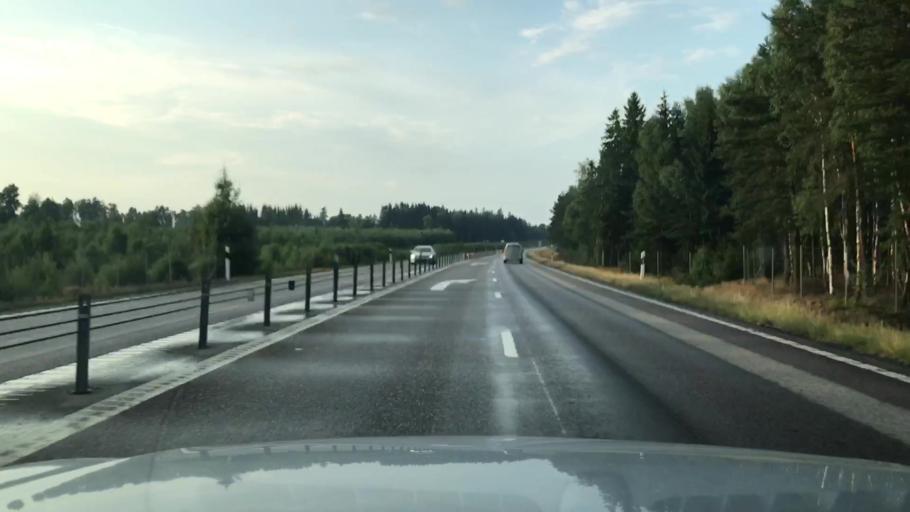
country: SE
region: Kronoberg
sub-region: Ljungby Kommun
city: Lagan
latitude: 56.8872
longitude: 13.9549
